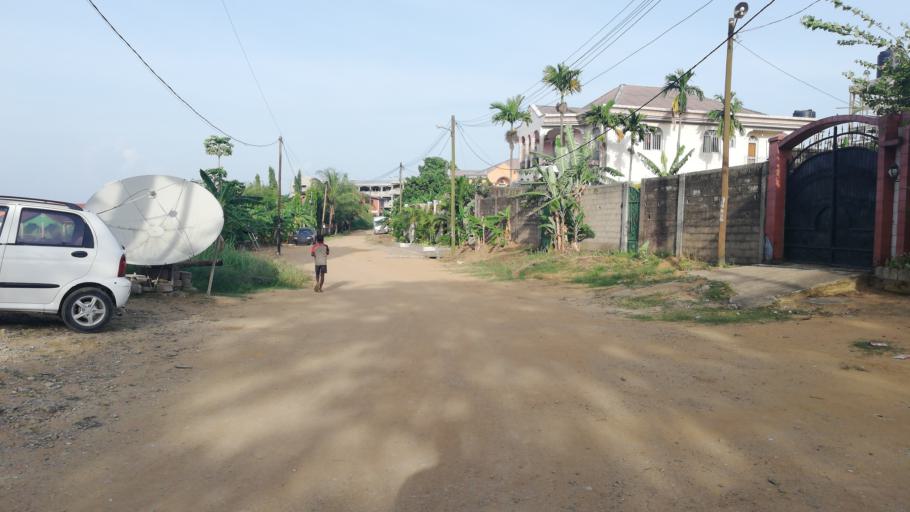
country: CM
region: Littoral
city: Douala
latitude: 4.1011
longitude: 9.7514
